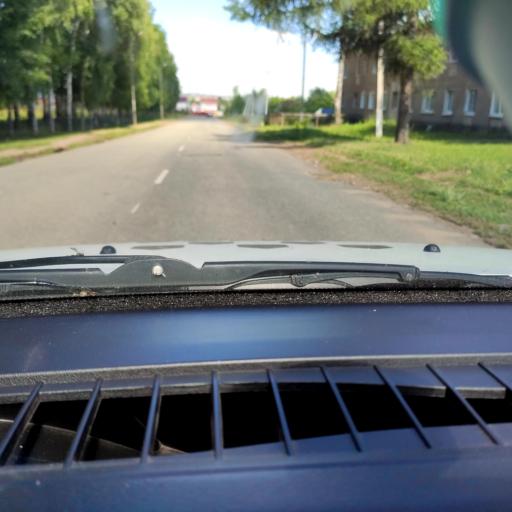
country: RU
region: Udmurtiya
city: Votkinsk
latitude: 57.0352
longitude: 53.9435
